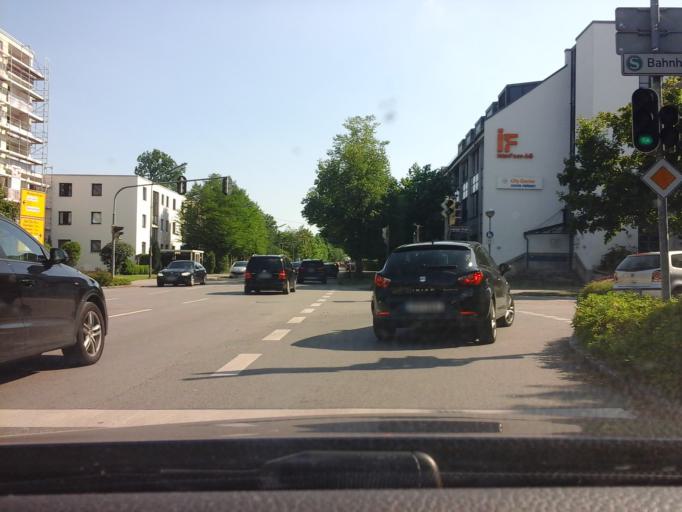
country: DE
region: Bavaria
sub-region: Upper Bavaria
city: Unterhaching
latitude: 48.0661
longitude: 11.6173
